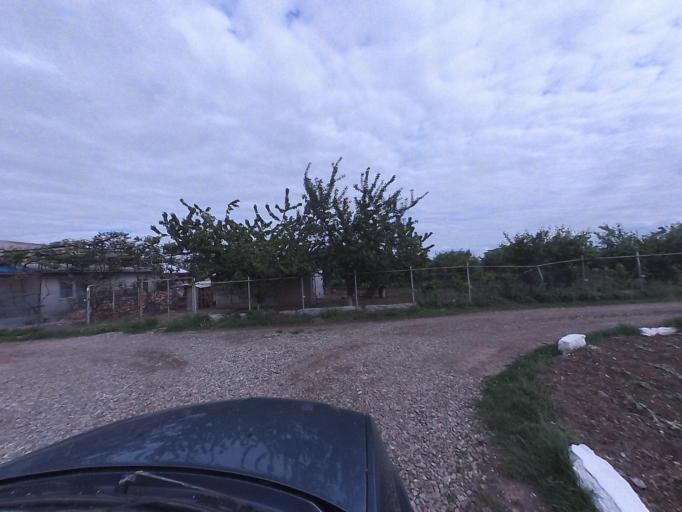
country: RO
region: Neamt
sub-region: Comuna Dulcesti
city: Dulcesti
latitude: 46.9575
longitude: 26.8013
